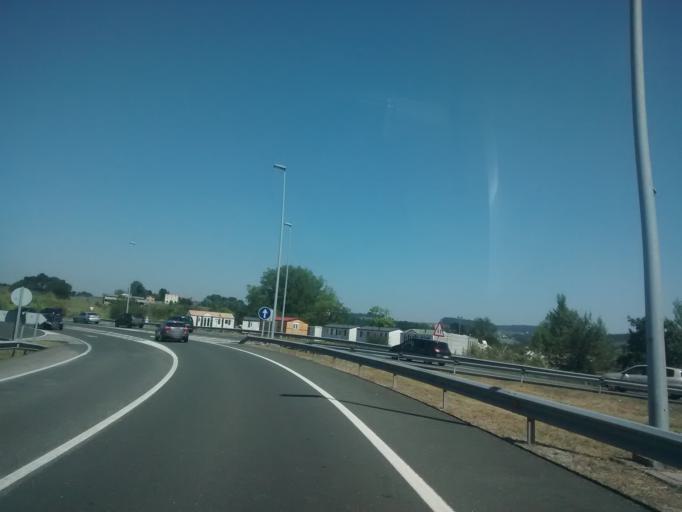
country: ES
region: Cantabria
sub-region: Provincia de Cantabria
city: Hazas de Cesto
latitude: 43.4118
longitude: -3.5660
